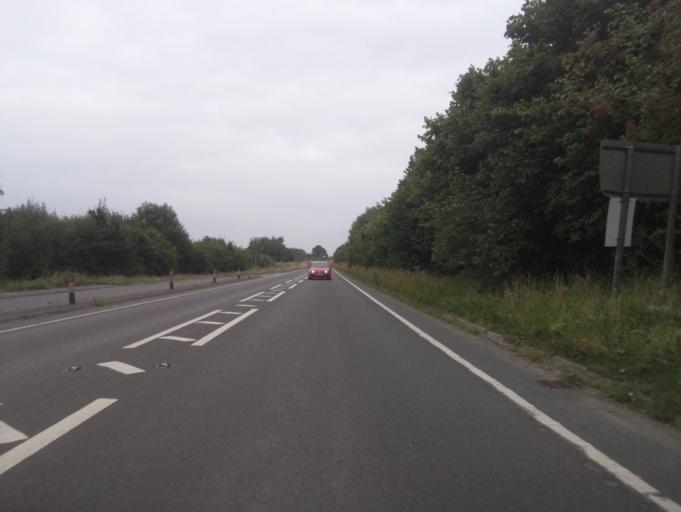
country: GB
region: England
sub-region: Shropshire
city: Stoke upon Tern
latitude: 52.8411
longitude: -2.5831
